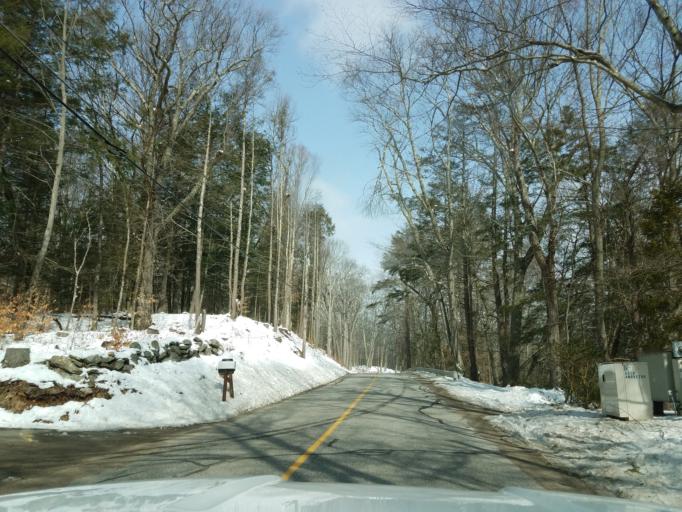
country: US
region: Connecticut
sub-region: Tolland County
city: Coventry Lake
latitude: 41.7281
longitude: -72.3584
